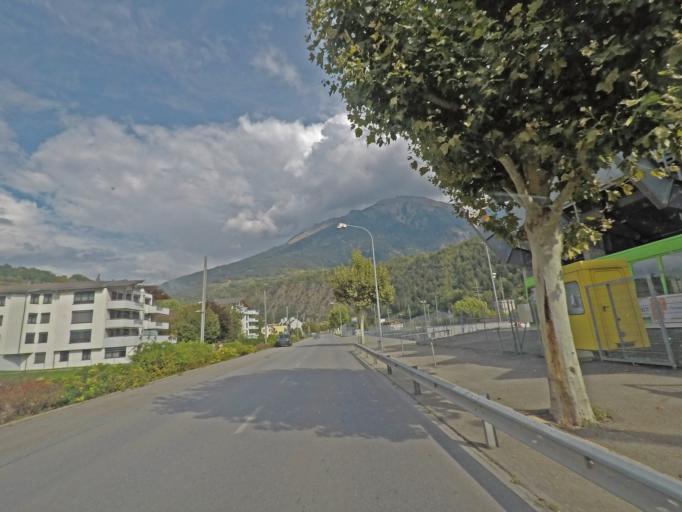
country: CH
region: Valais
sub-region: Brig District
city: Naters
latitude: 46.3261
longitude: 8.0025
